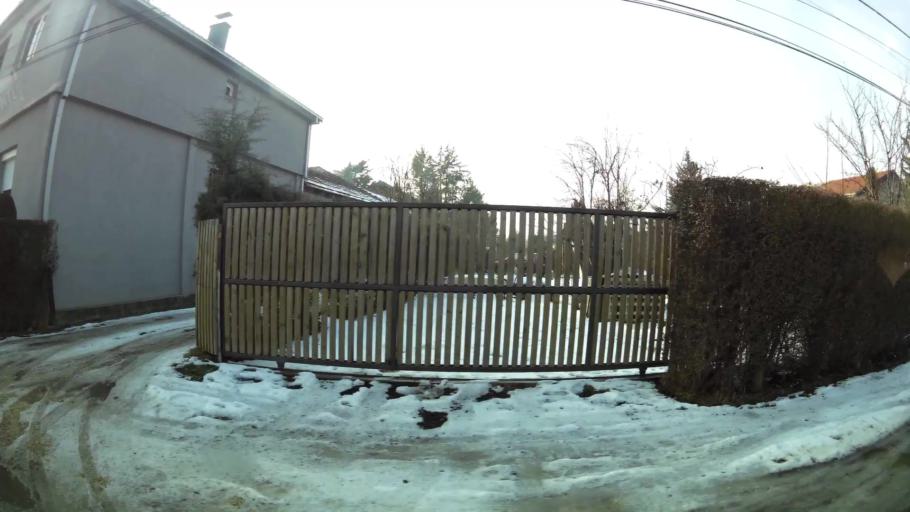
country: MK
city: Kadino
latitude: 41.9729
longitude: 21.5980
